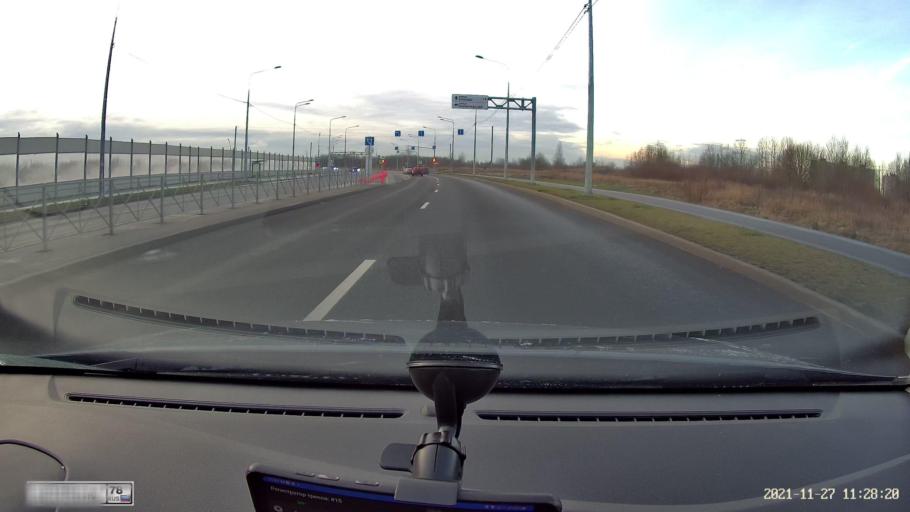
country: RU
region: St.-Petersburg
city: Krasnoye Selo
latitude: 59.7458
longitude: 30.0757
